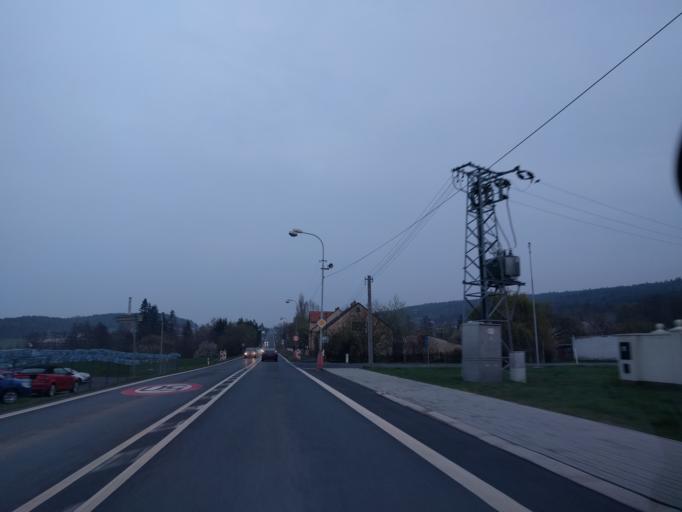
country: CZ
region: Ustecky
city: Lubenec
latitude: 50.1322
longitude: 13.3199
